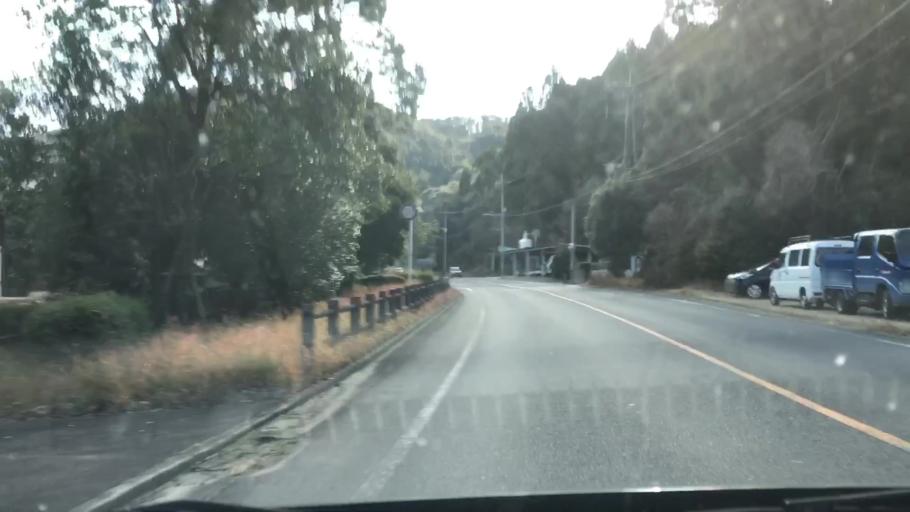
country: JP
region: Kagoshima
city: Satsumasendai
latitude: 31.8595
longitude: 130.3166
